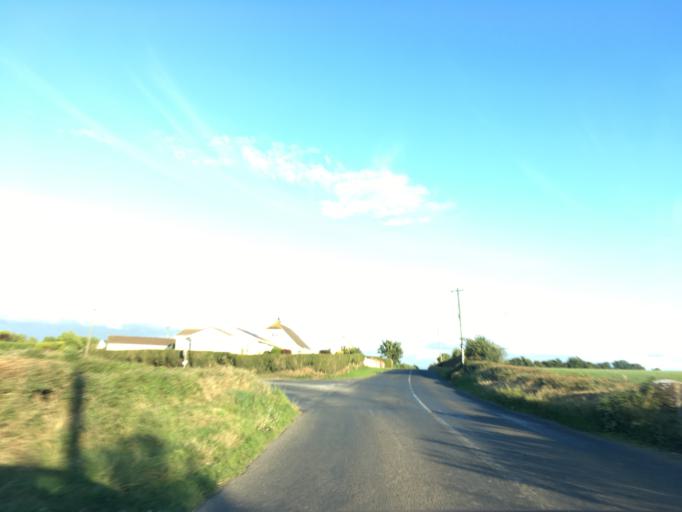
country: IE
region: Munster
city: Cashel
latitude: 52.4792
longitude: -7.9302
